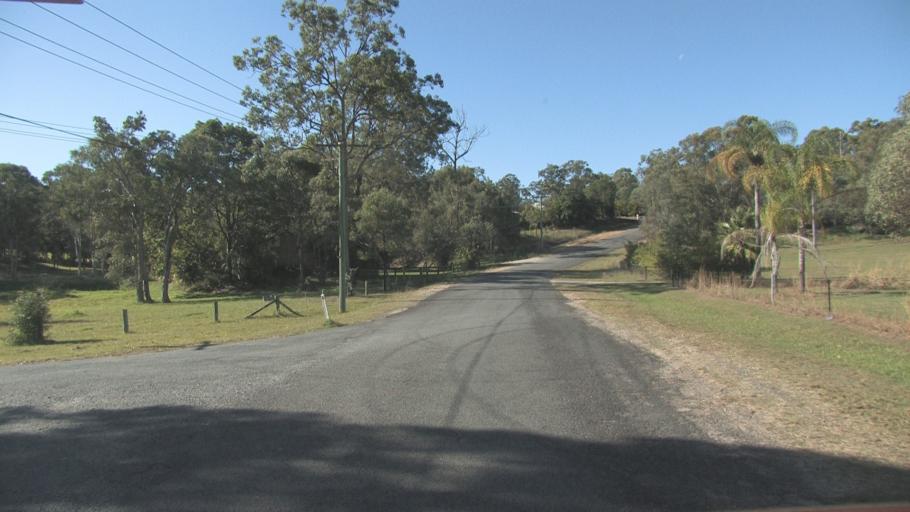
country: AU
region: Queensland
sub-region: Logan
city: Logan Reserve
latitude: -27.7430
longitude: 153.1333
